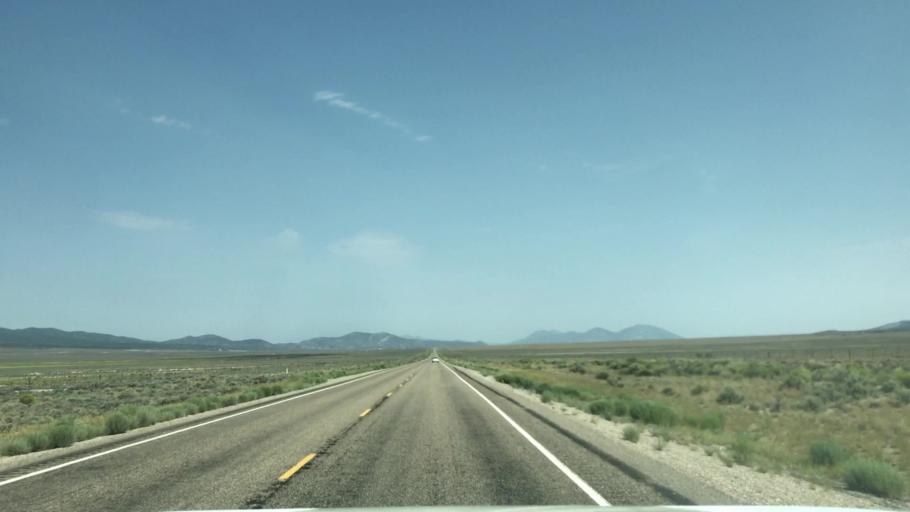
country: US
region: Nevada
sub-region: White Pine County
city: Ely
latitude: 39.1132
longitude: -114.7694
